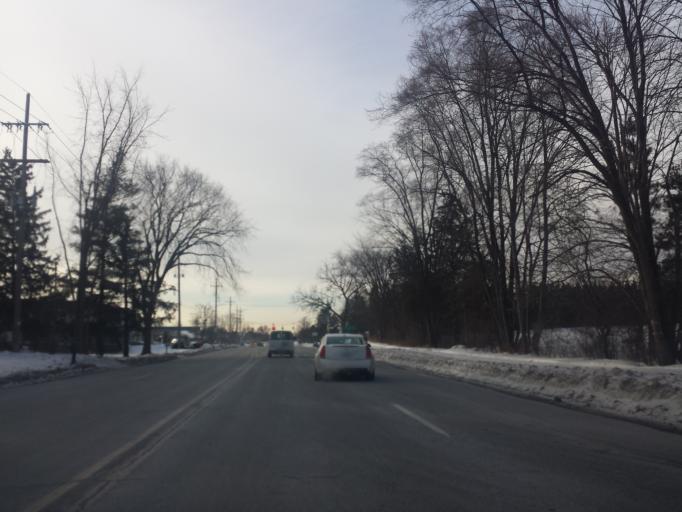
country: US
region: Michigan
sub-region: Oakland County
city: Franklin
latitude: 42.5015
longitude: -83.3392
